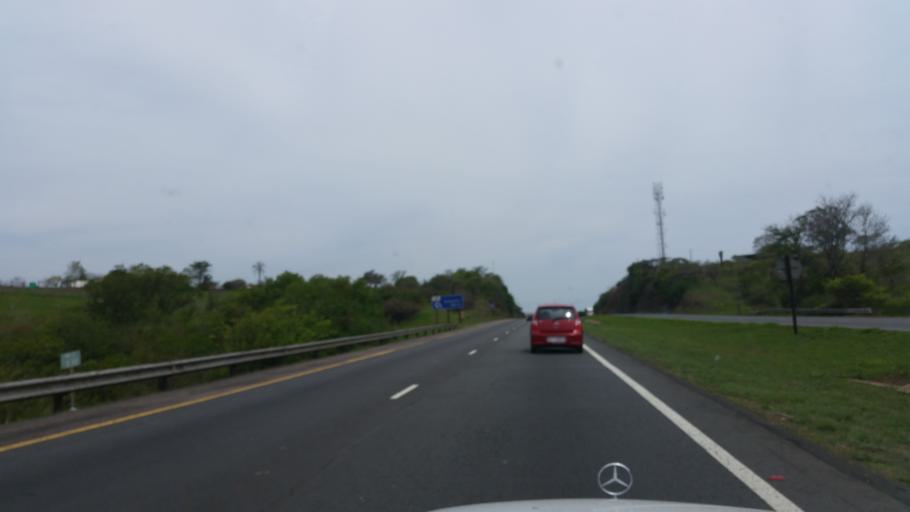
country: ZA
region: KwaZulu-Natal
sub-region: uMgungundlovu District Municipality
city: Pietermaritzburg
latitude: -29.6563
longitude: 30.4524
